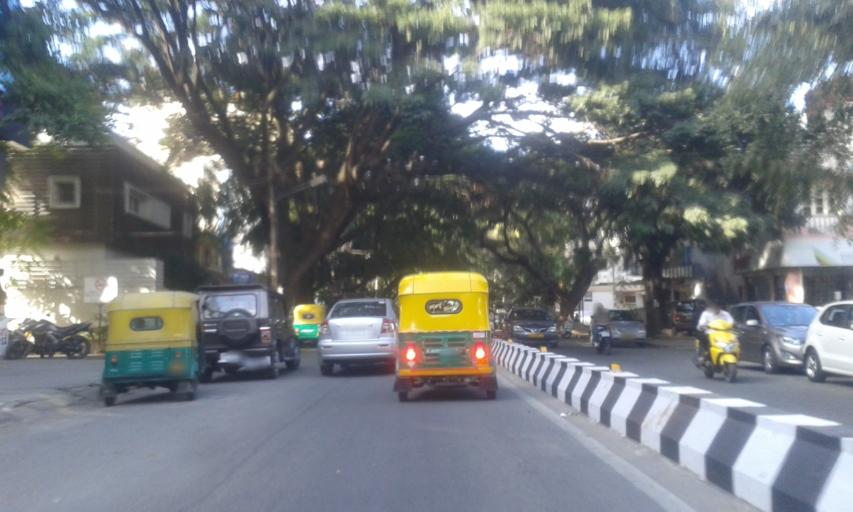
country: IN
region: Karnataka
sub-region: Bangalore Urban
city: Bangalore
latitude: 12.9222
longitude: 77.5895
